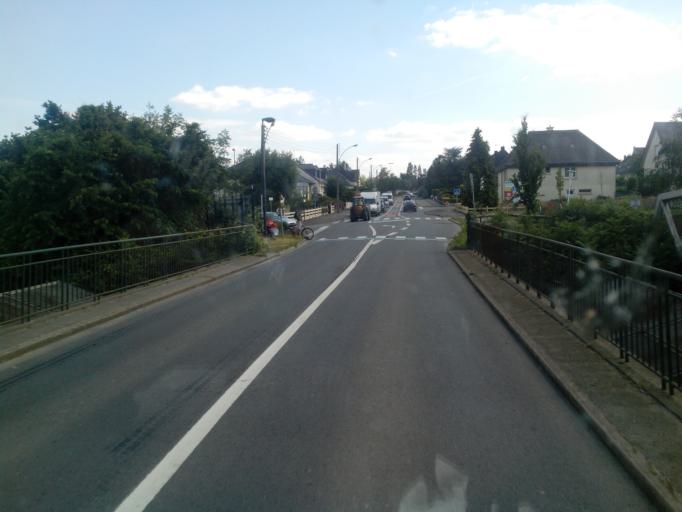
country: FR
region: Brittany
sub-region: Departement d'Ille-et-Vilaine
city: Noyal-sur-Vilaine
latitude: 48.1194
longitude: -1.5319
